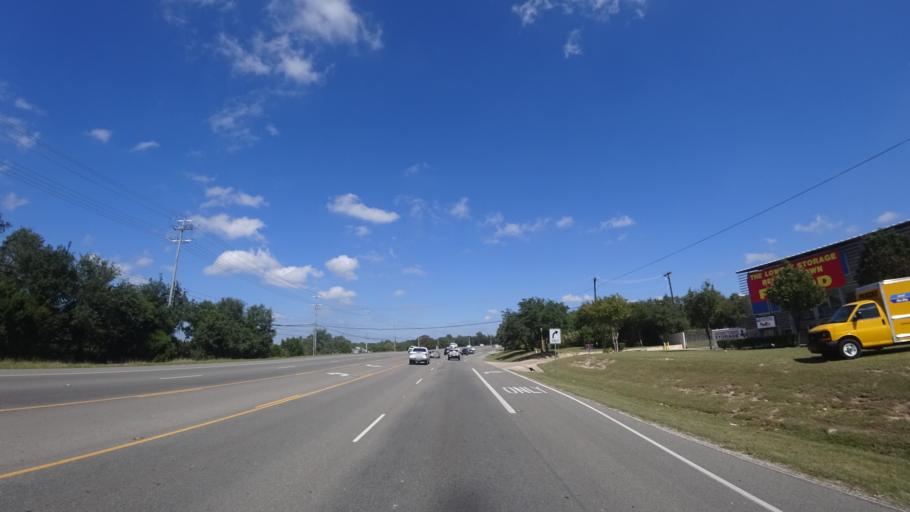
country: US
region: Texas
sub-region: Williamson County
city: Anderson Mill
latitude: 30.4334
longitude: -97.8410
